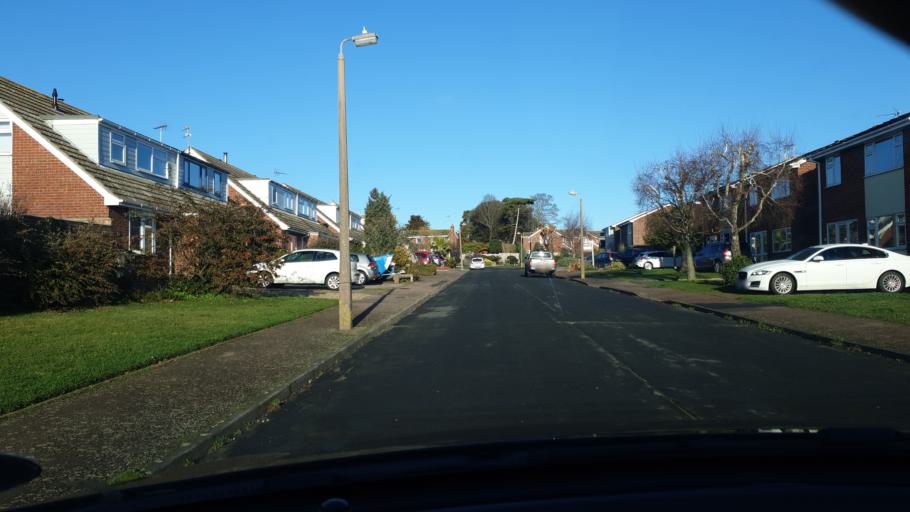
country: GB
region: England
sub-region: Essex
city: Brightlingsea
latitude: 51.8152
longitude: 1.0193
